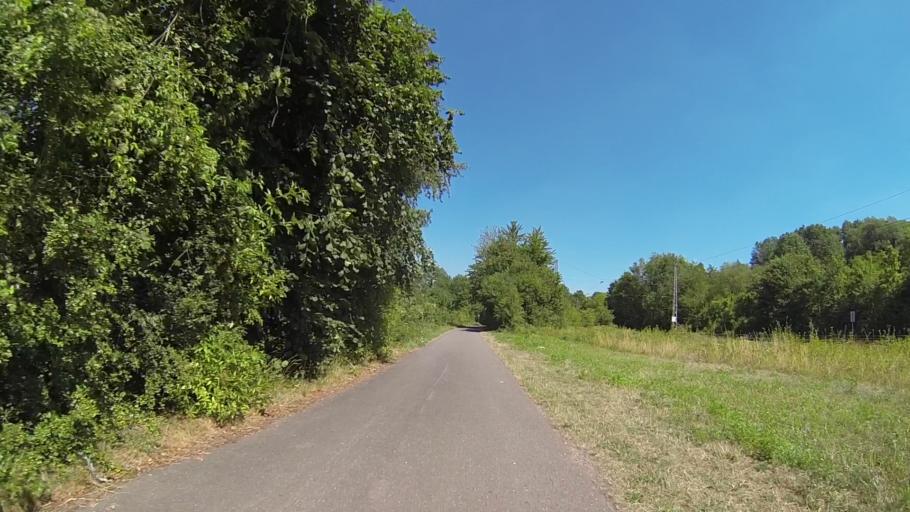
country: LU
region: Grevenmacher
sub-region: Canton de Grevenmacher
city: Wormeldange
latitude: 49.6111
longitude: 6.4095
